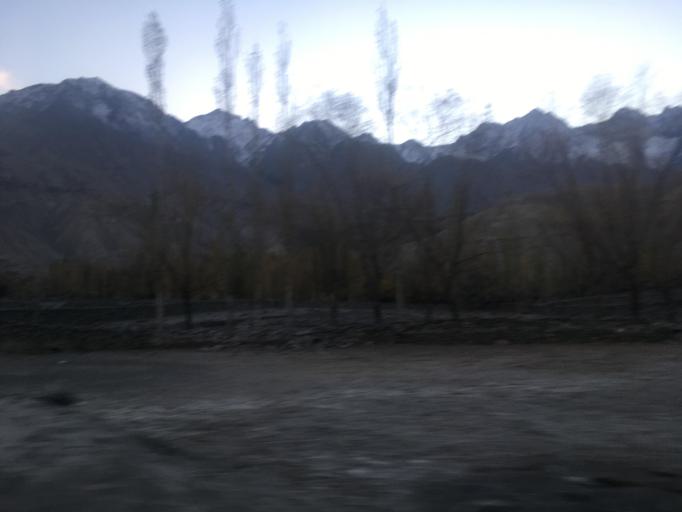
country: PK
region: Gilgit-Baltistan
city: Skardu
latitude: 35.3039
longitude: 75.5372
